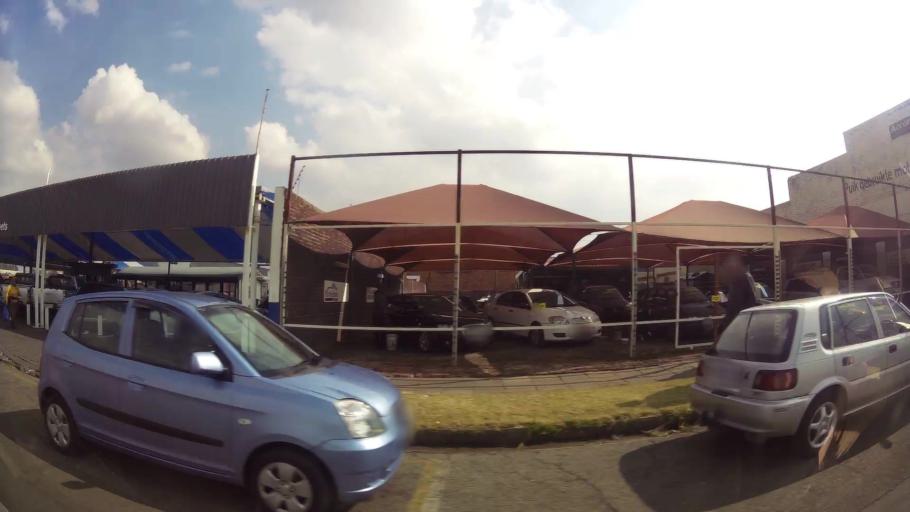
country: ZA
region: Gauteng
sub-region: Sedibeng District Municipality
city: Vereeniging
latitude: -26.6839
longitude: 27.9294
